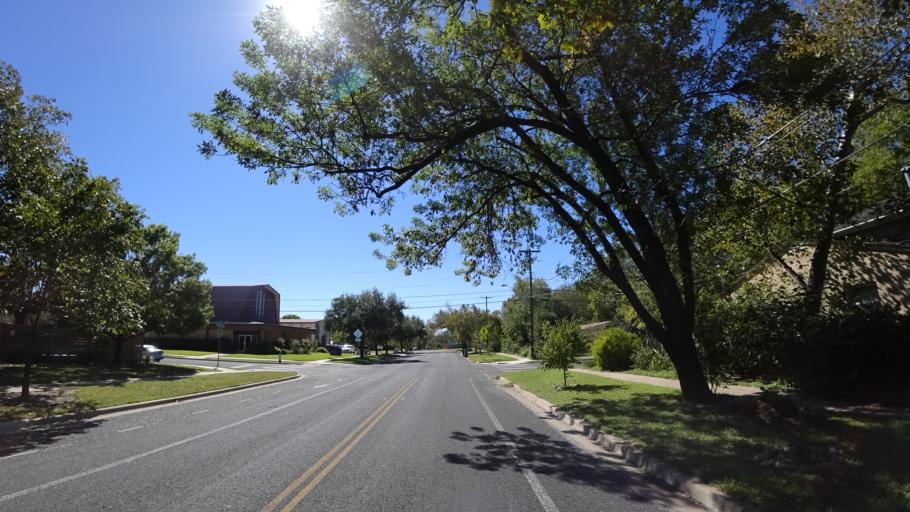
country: US
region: Texas
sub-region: Travis County
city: Austin
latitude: 30.3354
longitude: -97.7297
